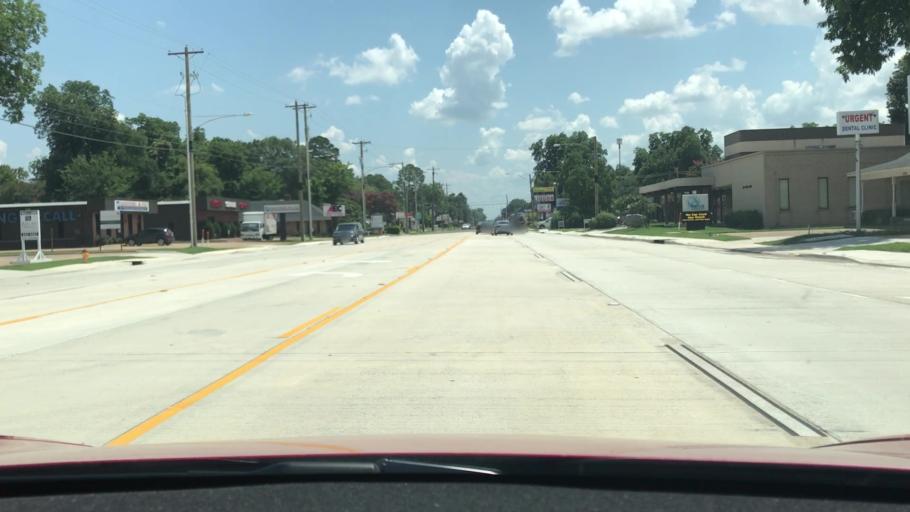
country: US
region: Louisiana
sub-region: Bossier Parish
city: Bossier City
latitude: 32.4784
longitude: -93.7222
